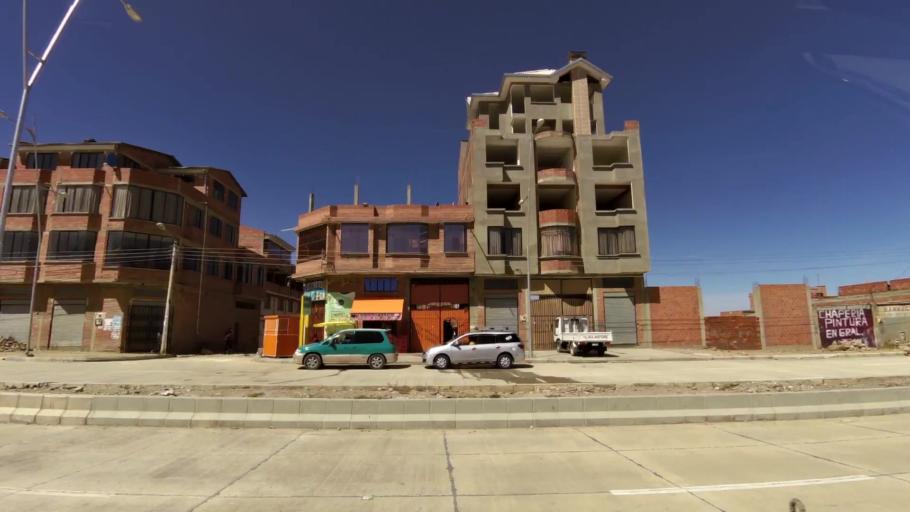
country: BO
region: La Paz
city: La Paz
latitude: -16.4964
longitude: -68.2257
